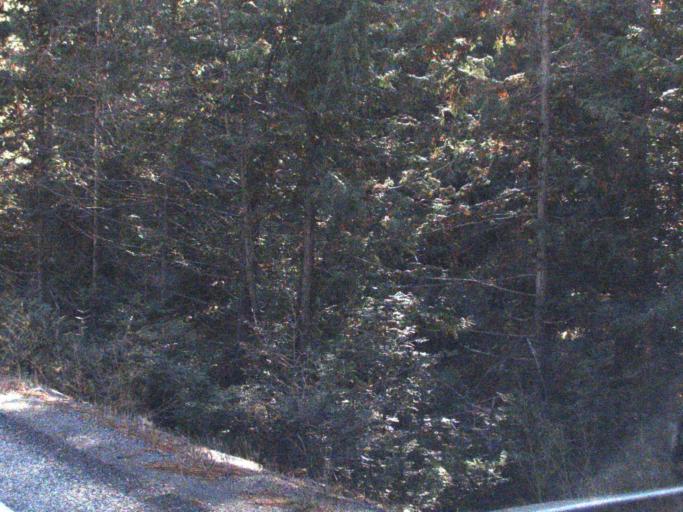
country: US
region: Washington
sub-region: Stevens County
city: Kettle Falls
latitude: 48.5991
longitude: -118.3502
